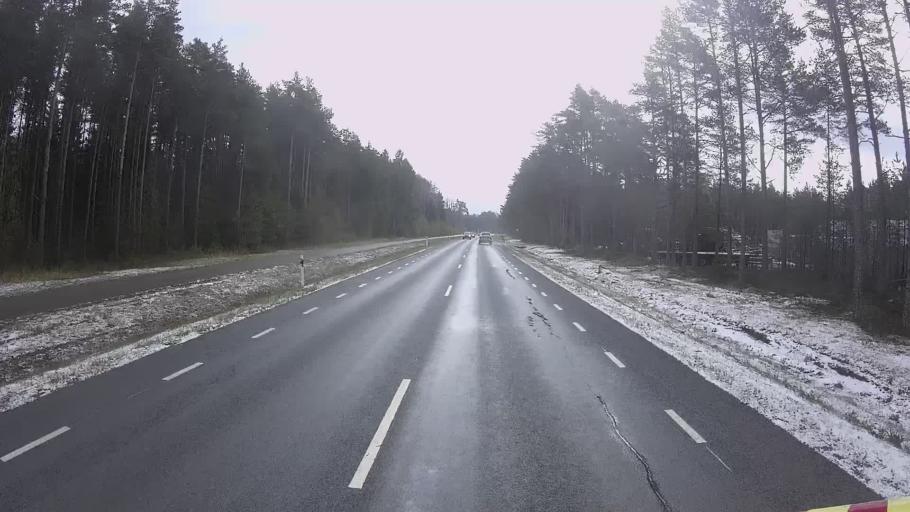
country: EE
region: Hiiumaa
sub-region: Kaerdla linn
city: Kardla
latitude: 58.9967
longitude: 22.7123
